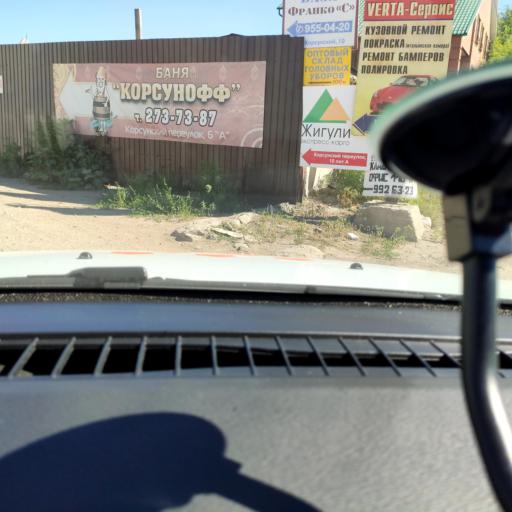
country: RU
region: Samara
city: Smyshlyayevka
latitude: 53.2127
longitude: 50.2760
